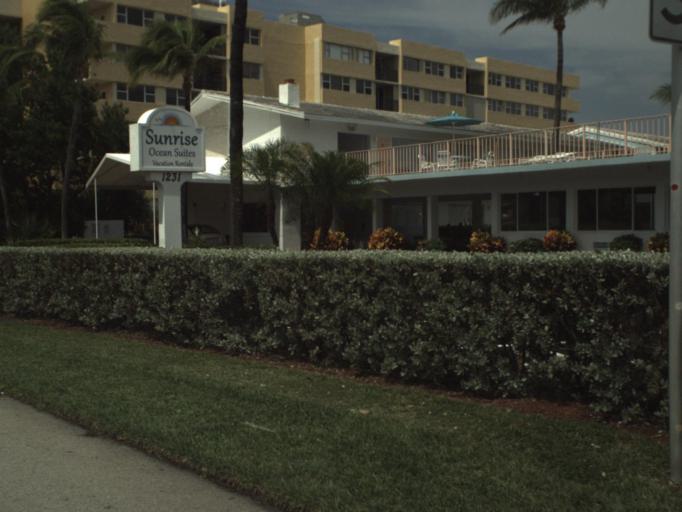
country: US
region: Florida
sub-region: Broward County
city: Hillsboro Beach
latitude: 26.3041
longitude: -80.0776
